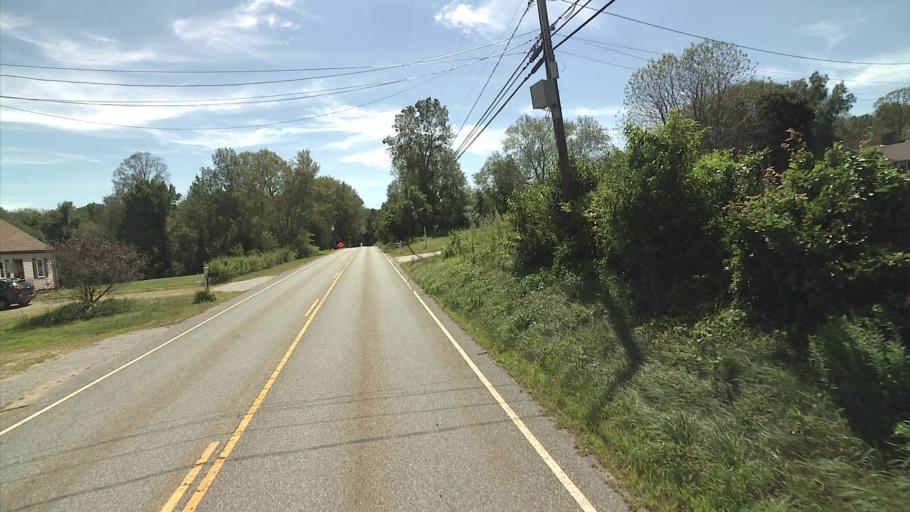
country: US
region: Connecticut
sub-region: Windham County
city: South Woodstock
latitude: 41.8419
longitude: -72.0169
